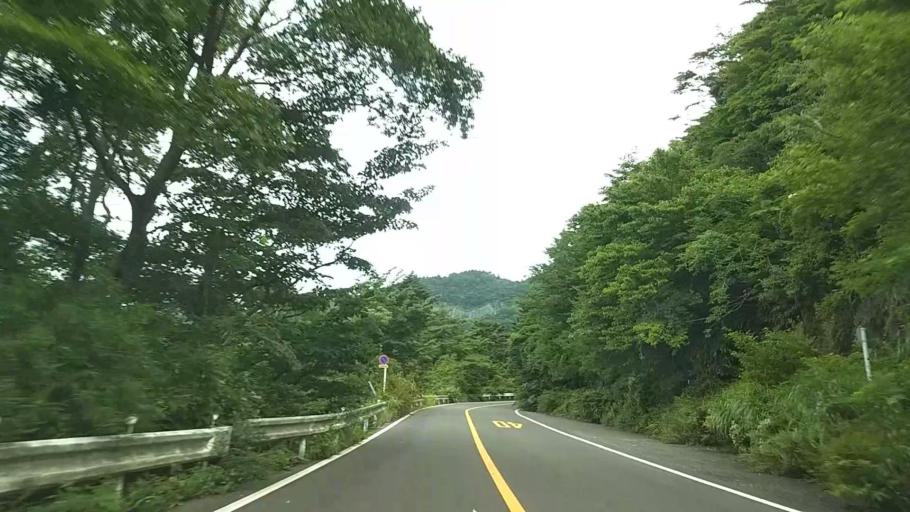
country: JP
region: Kanagawa
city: Yugawara
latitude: 35.1756
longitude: 139.0642
